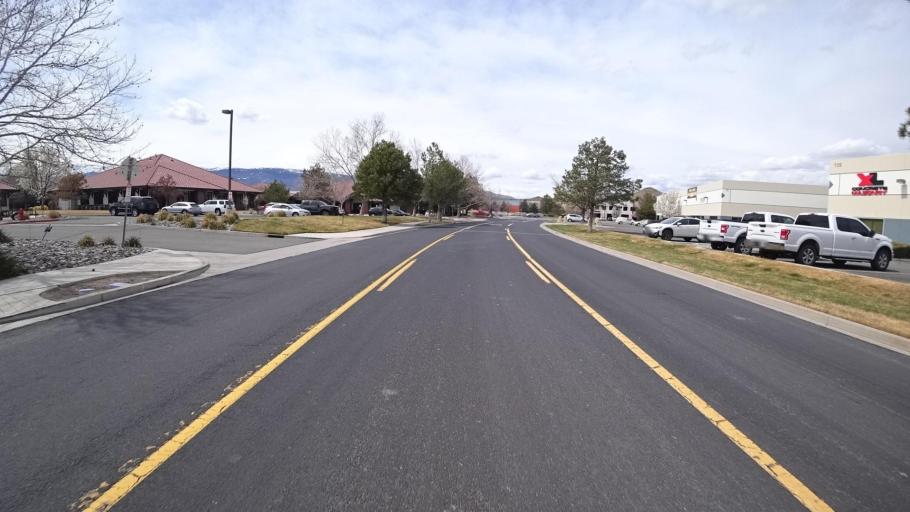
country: US
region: Nevada
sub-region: Washoe County
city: Sparks
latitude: 39.4481
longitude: -119.7581
